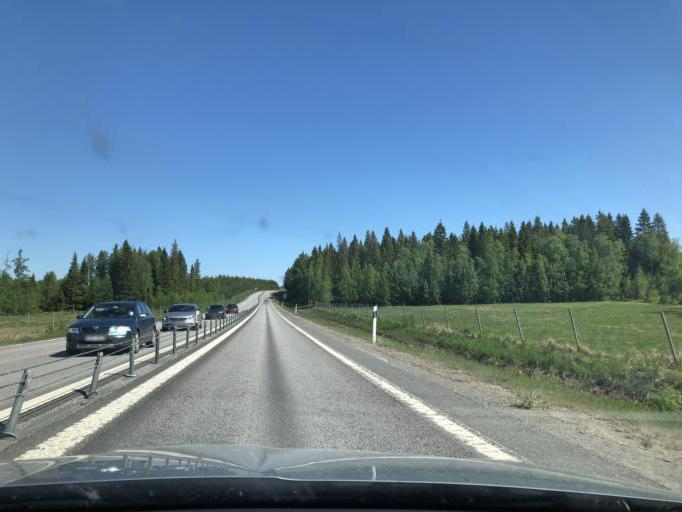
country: SE
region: Norrbotten
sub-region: Lulea Kommun
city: Lulea
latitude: 65.6991
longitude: 22.1171
